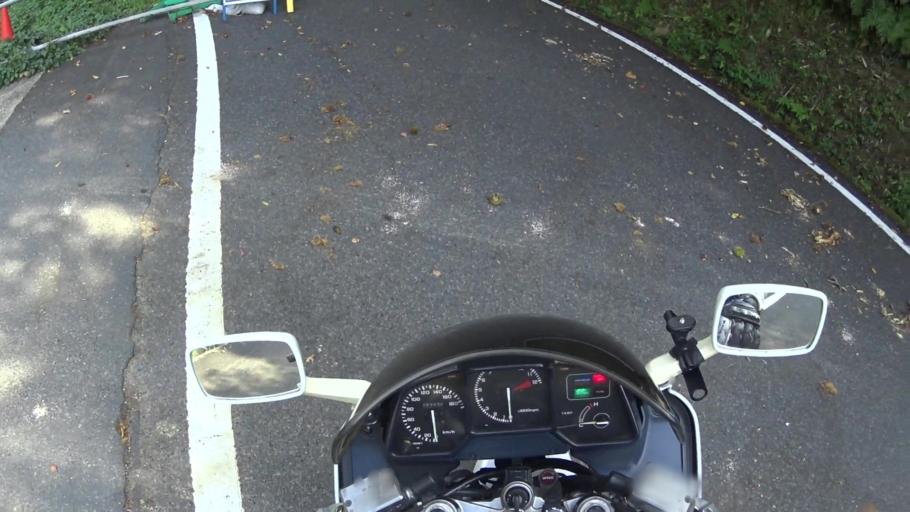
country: JP
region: Kyoto
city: Miyazu
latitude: 35.6769
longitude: 135.2707
